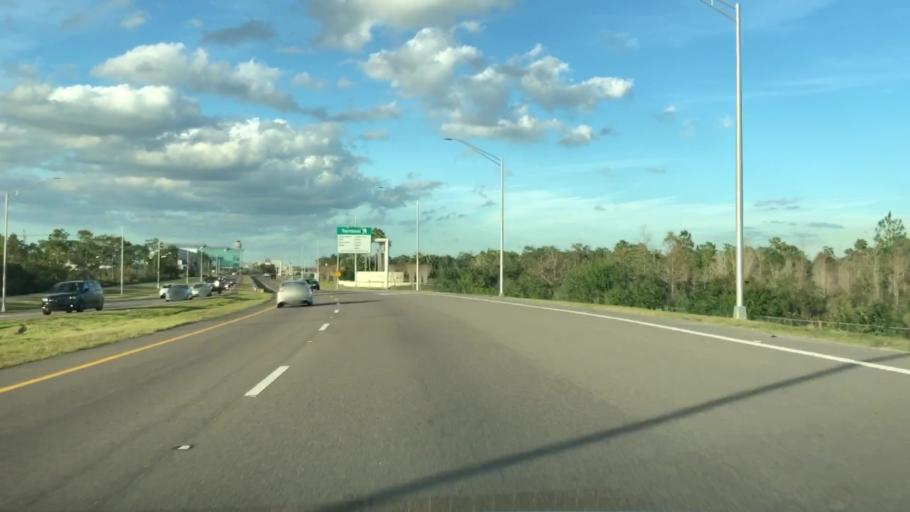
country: US
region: Florida
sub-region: Orange County
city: Meadow Woods
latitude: 28.4023
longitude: -81.3073
